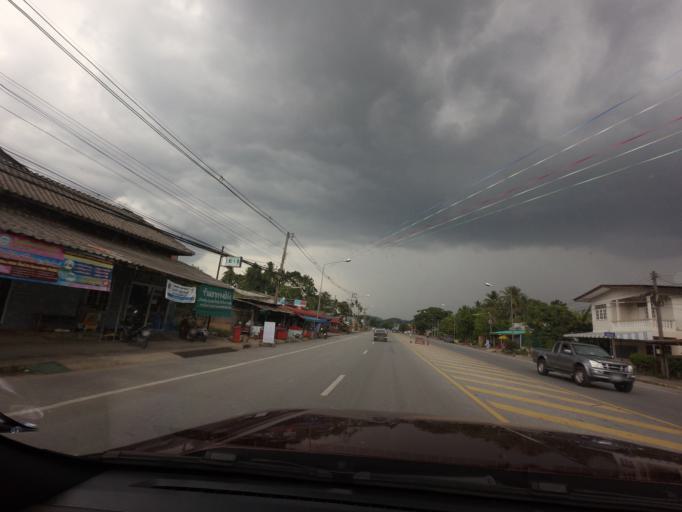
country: TH
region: Yala
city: Krong Pi Nang
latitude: 6.4177
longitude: 101.2793
